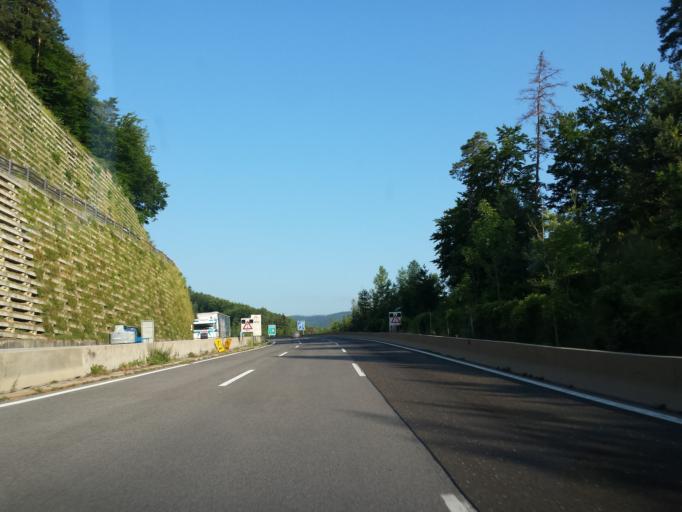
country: AT
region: Lower Austria
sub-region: Politischer Bezirk Neunkirchen
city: Schottwien
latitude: 47.6544
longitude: 15.8863
